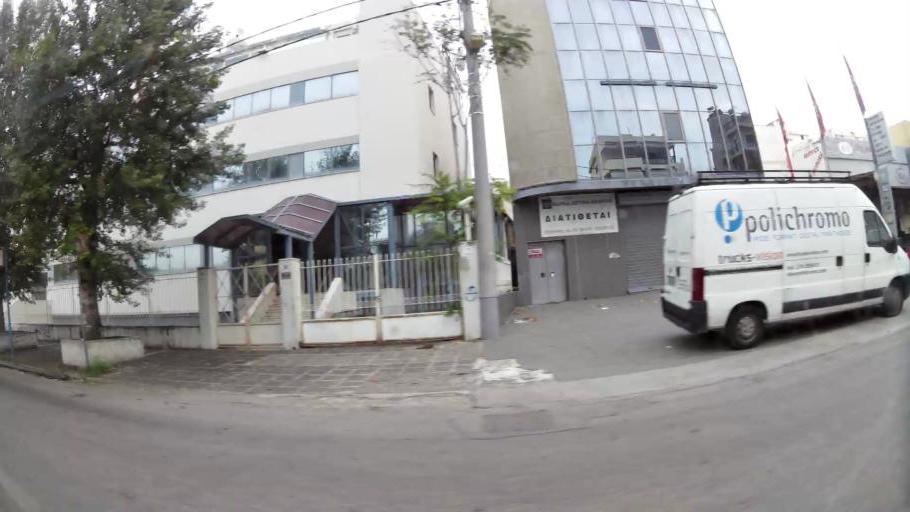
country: GR
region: Attica
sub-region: Nomarchia Athinas
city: Peristeri
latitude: 38.0073
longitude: 23.7067
